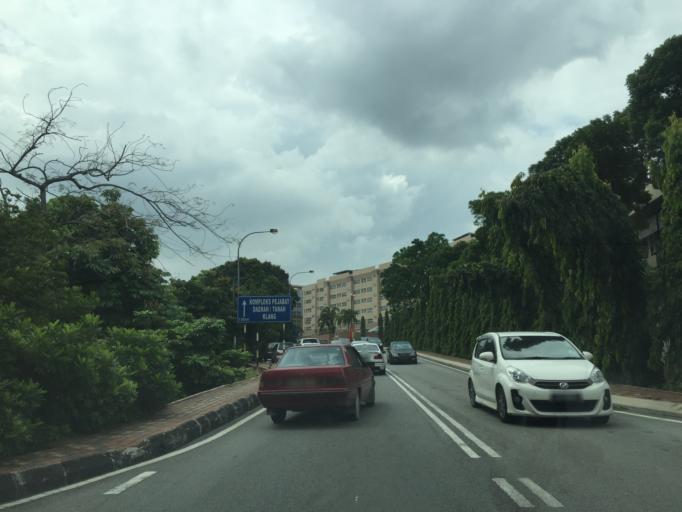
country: MY
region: Selangor
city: Klang
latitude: 3.0431
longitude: 101.4444
